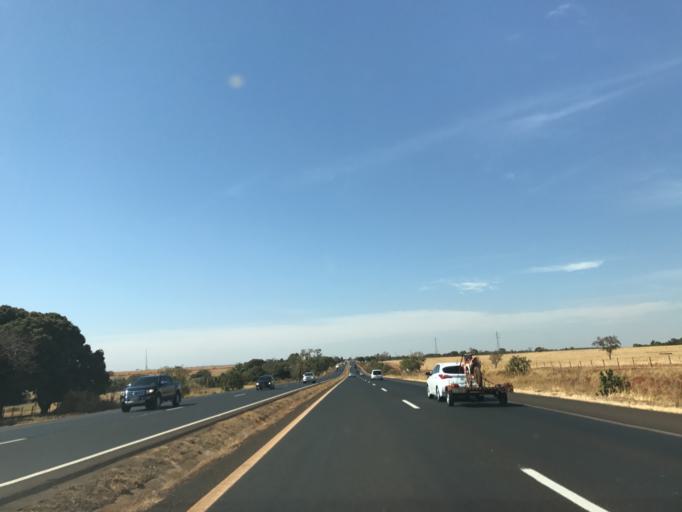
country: BR
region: Minas Gerais
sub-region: Centralina
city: Centralina
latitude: -18.6900
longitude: -49.1499
